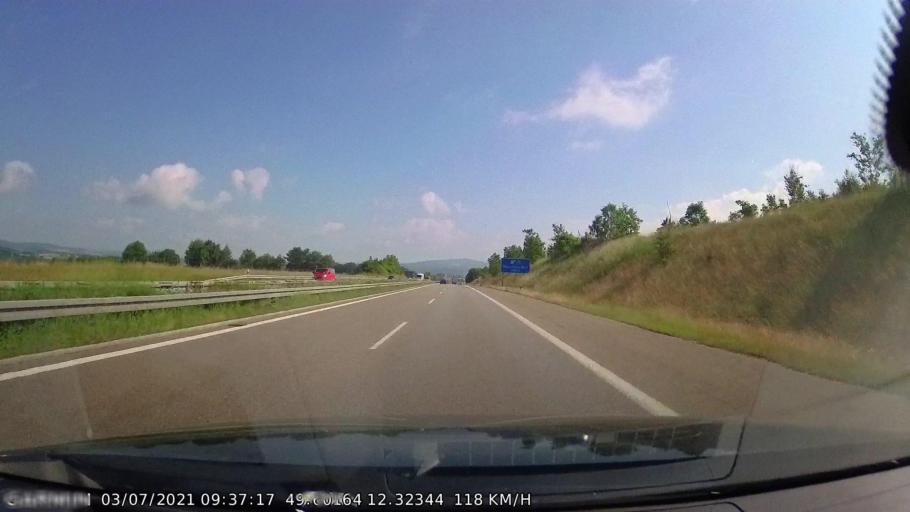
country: DE
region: Bavaria
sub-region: Upper Palatinate
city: Vohenstrauss
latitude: 49.6017
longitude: 12.3235
